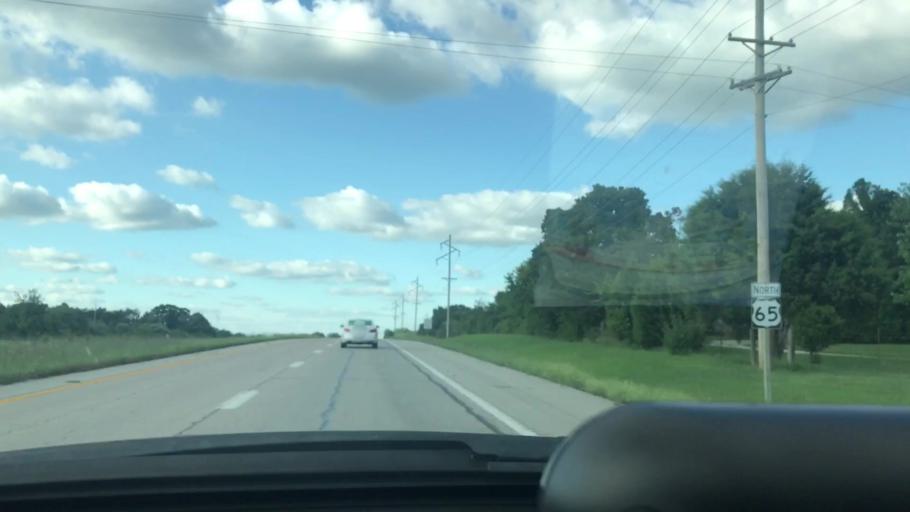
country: US
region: Missouri
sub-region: Pettis County
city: Sedalia
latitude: 38.6264
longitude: -93.2672
